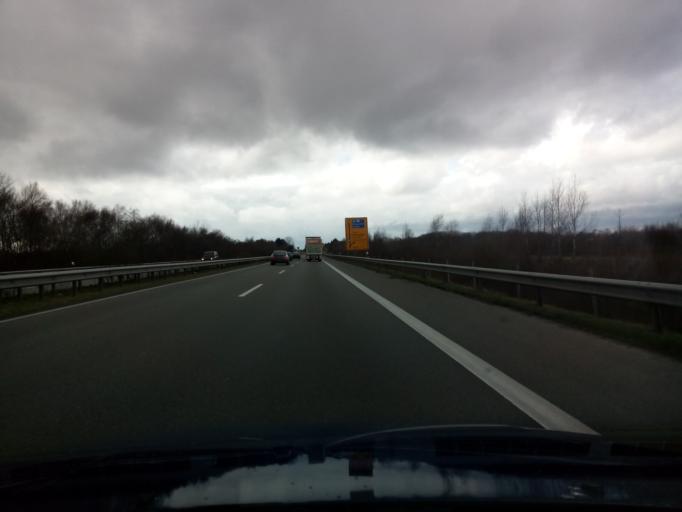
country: DE
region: Lower Saxony
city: Twist
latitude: 52.7226
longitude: 7.1107
